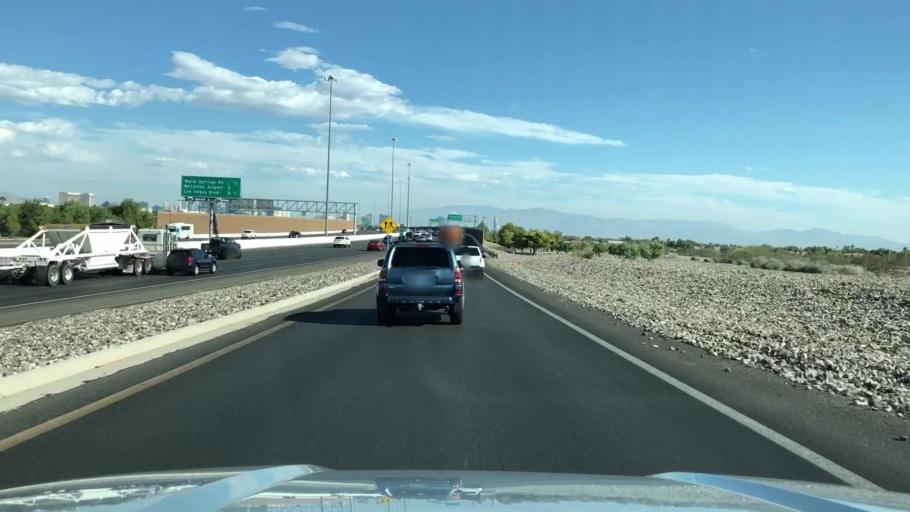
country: US
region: Nevada
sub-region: Clark County
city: Paradise
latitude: 36.0442
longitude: -115.1337
